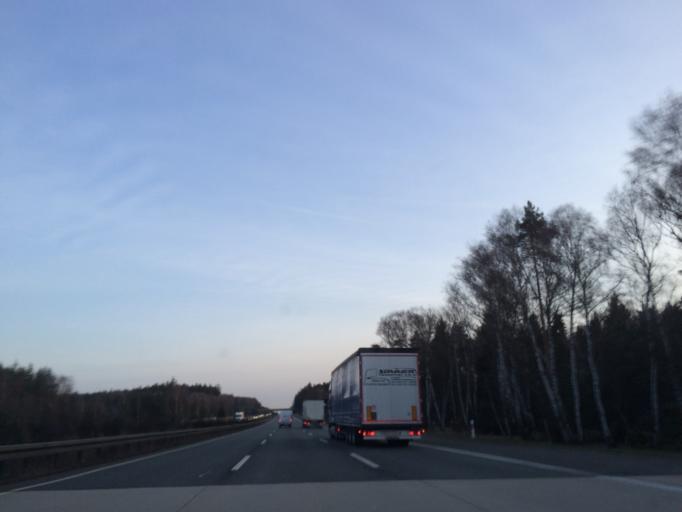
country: DE
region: Thuringia
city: Bad Klosterlausnitz
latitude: 50.9230
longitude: 11.8398
